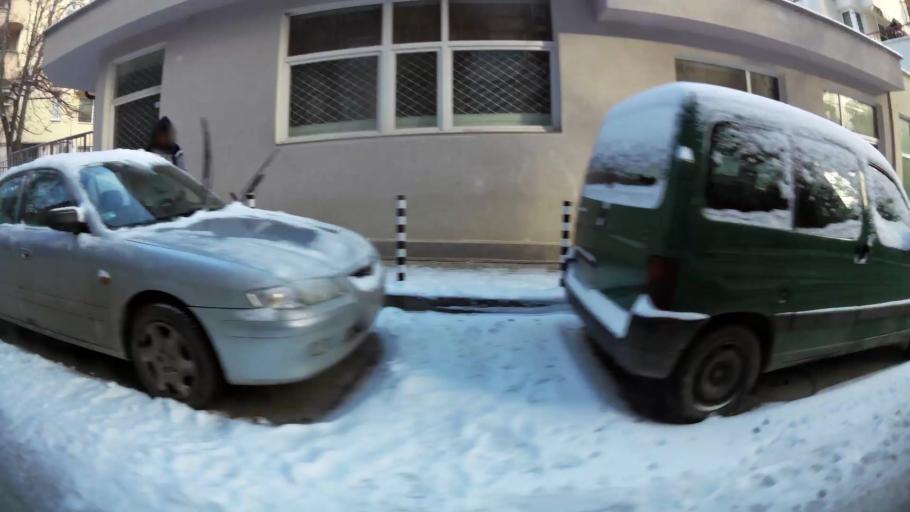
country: BG
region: Sofia-Capital
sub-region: Stolichna Obshtina
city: Sofia
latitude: 42.6724
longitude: 23.3327
